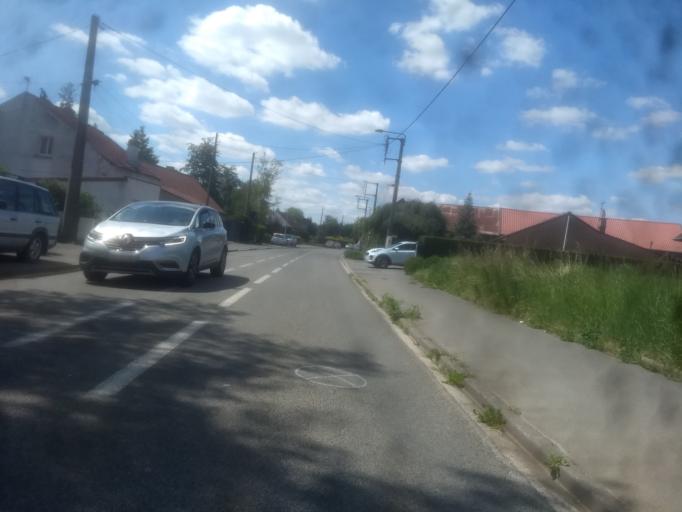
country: FR
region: Nord-Pas-de-Calais
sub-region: Departement du Pas-de-Calais
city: Dainville
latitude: 50.2497
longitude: 2.7299
